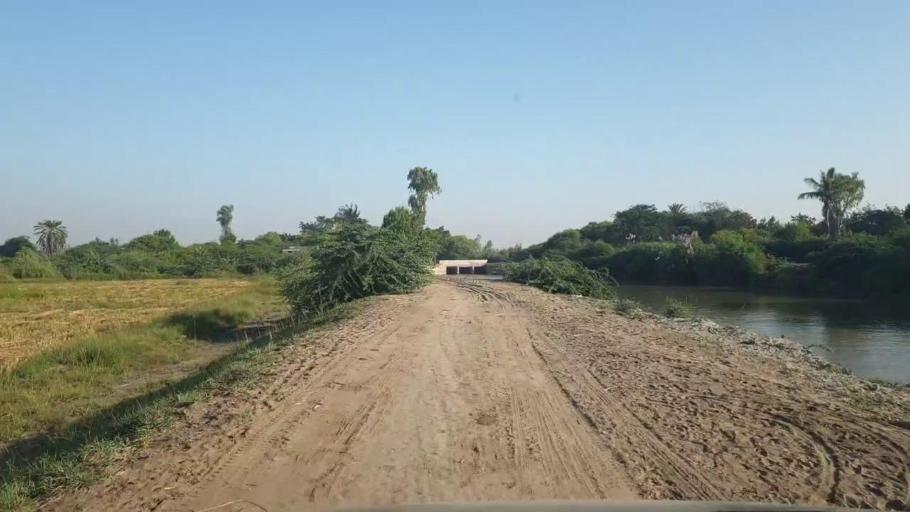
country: PK
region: Sindh
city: Badin
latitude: 24.6878
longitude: 68.8159
